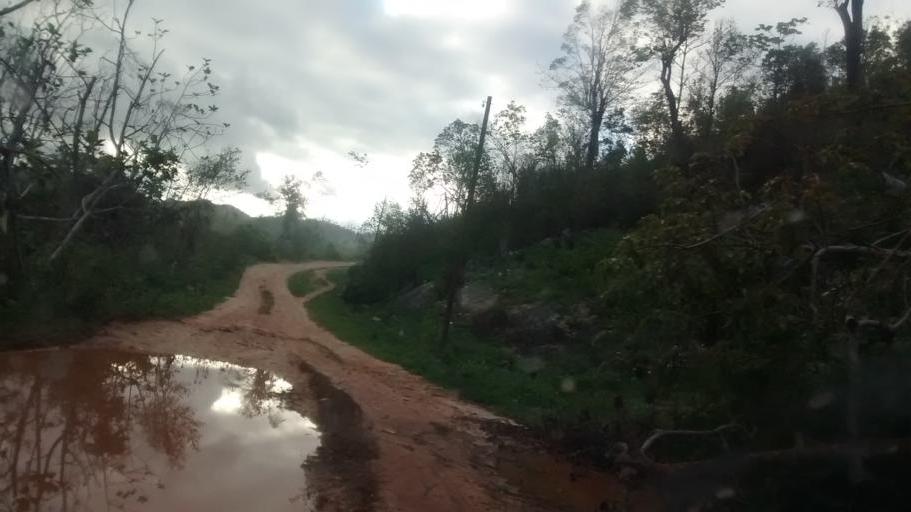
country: HT
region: Grandans
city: Corail
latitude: 18.4796
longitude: -73.8072
